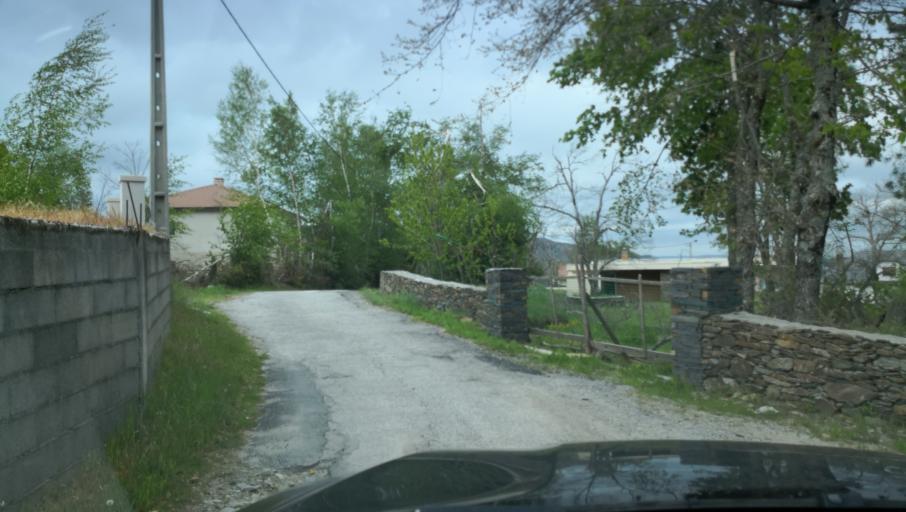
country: PT
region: Vila Real
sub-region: Santa Marta de Penaguiao
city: Santa Marta de Penaguiao
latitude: 41.2837
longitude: -7.8715
